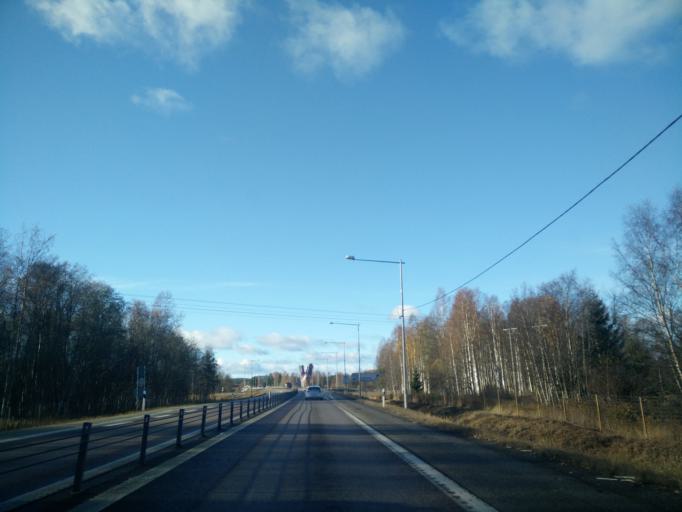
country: SE
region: Vaesternorrland
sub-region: Timra Kommun
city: Bergeforsen
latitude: 62.5175
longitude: 17.4445
